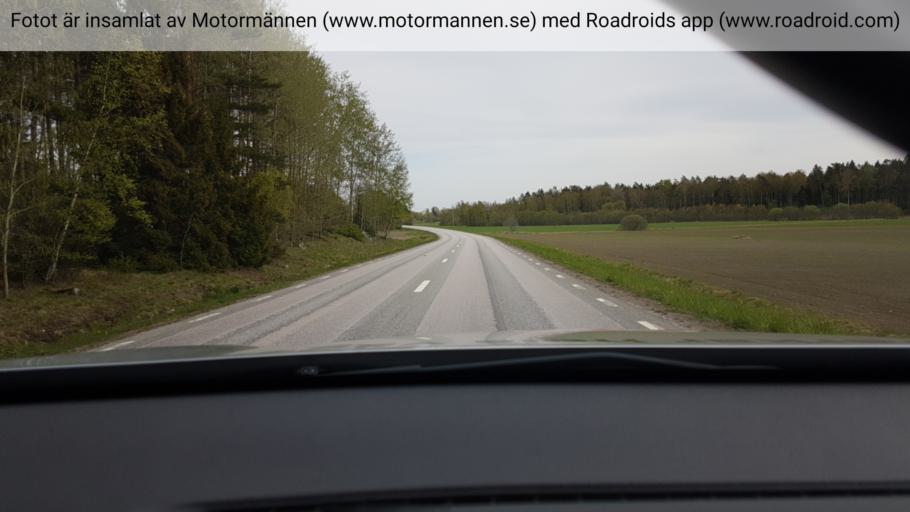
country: SE
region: Uppsala
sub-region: Osthammars Kommun
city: Gimo
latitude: 59.9601
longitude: 18.1063
